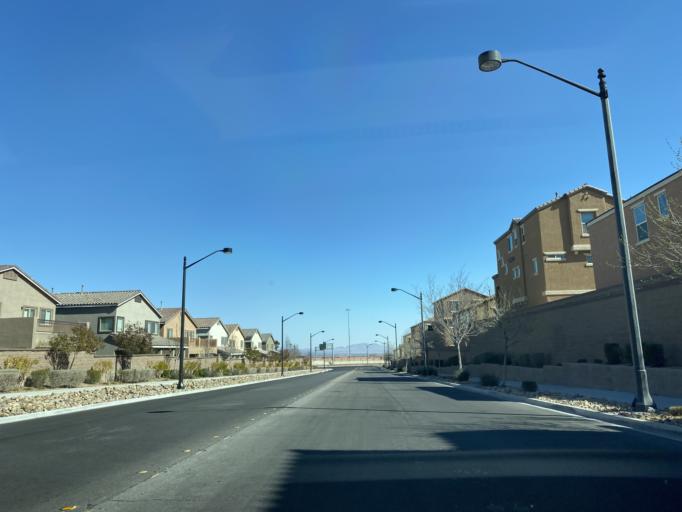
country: US
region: Nevada
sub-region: Clark County
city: Summerlin South
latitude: 36.3028
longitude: -115.2935
